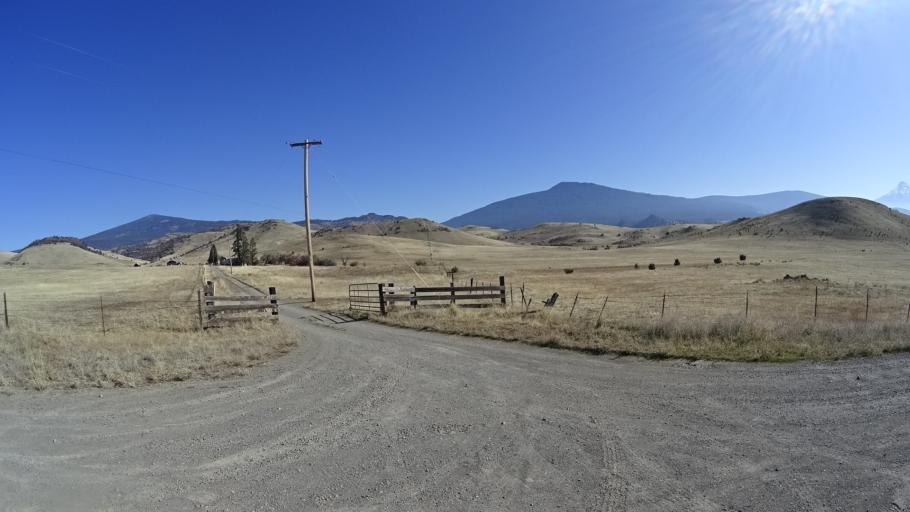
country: US
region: California
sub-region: Siskiyou County
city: Montague
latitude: 41.7637
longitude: -122.3569
